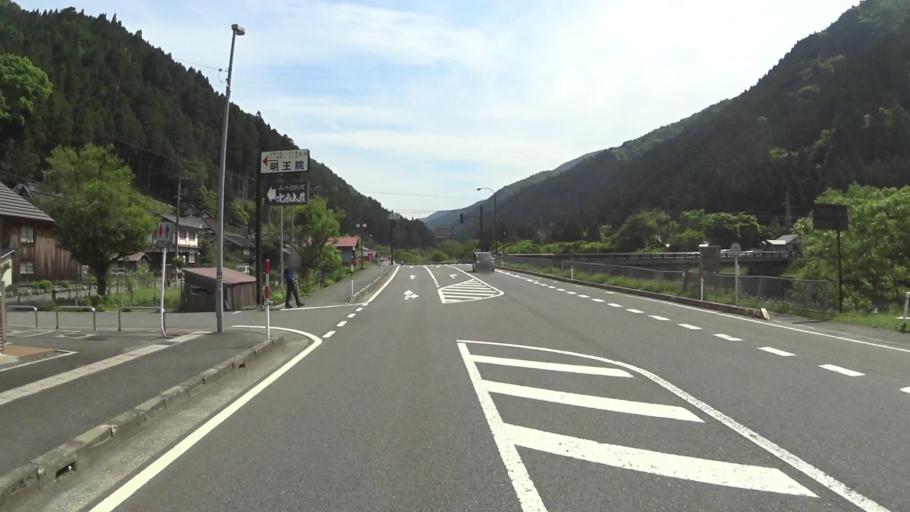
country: JP
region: Shiga Prefecture
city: Kitahama
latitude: 35.2473
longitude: 135.8676
